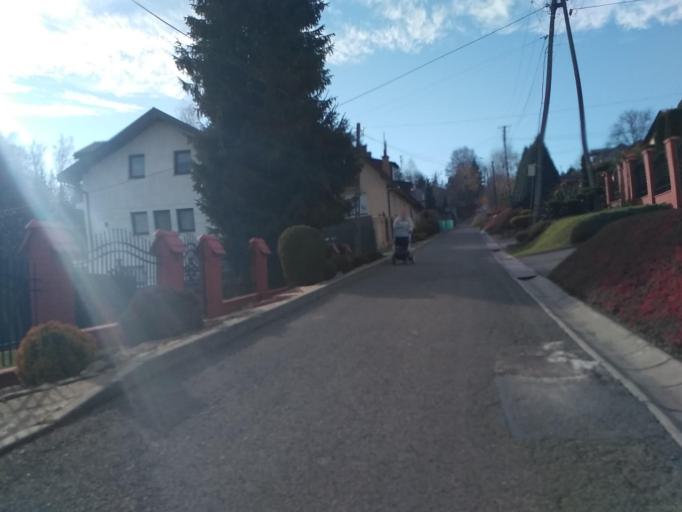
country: PL
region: Subcarpathian Voivodeship
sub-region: Powiat brzozowski
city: Brzozow
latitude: 49.6947
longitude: 22.0130
